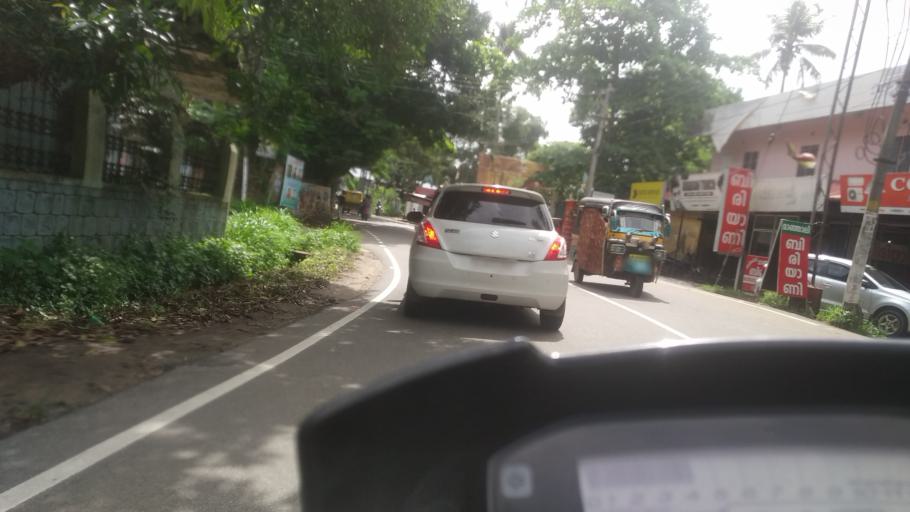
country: IN
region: Kerala
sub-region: Ernakulam
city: Elur
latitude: 10.1456
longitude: 76.2574
